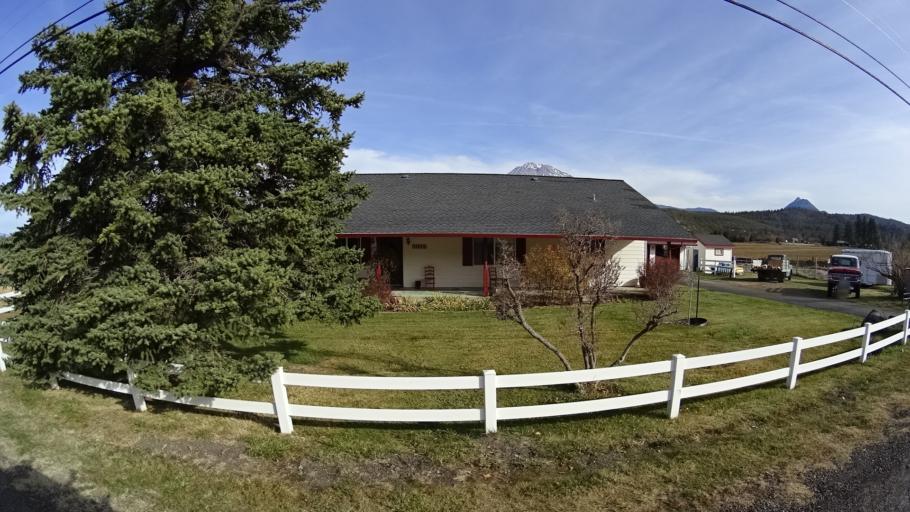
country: US
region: California
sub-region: Siskiyou County
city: Weed
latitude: 41.4244
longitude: -122.4369
